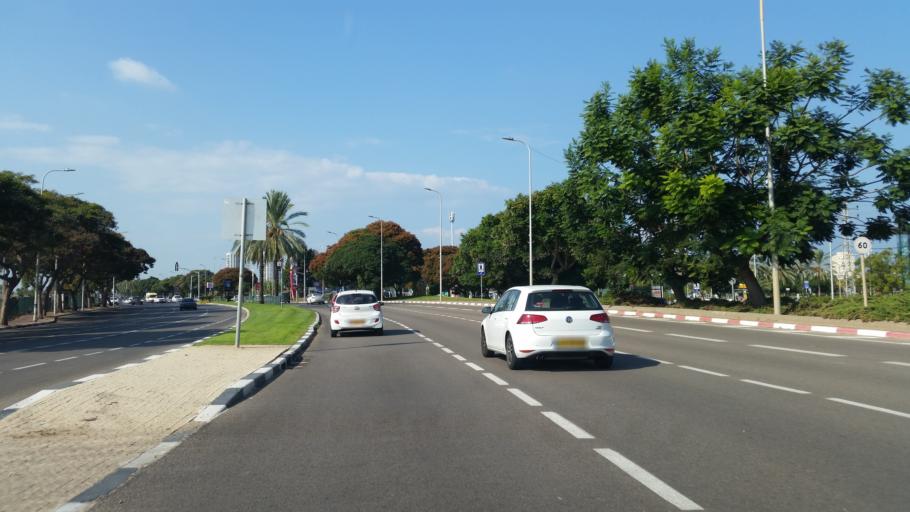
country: IL
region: Tel Aviv
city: Herzliyya
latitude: 32.1636
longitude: 34.8248
